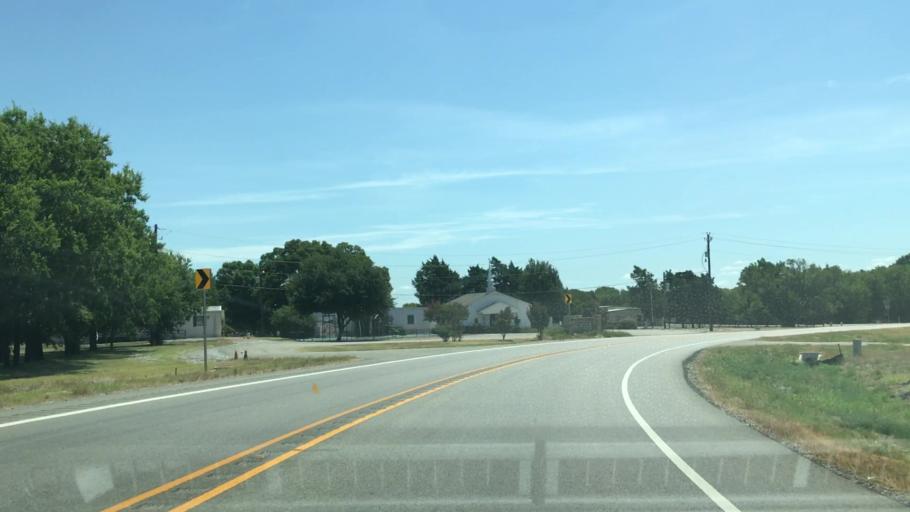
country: US
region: Texas
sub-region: Collin County
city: Fairview
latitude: 33.1198
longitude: -96.6060
